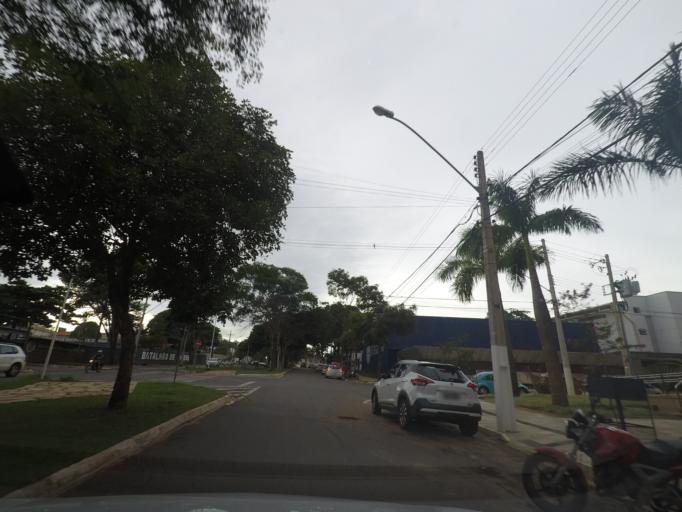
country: BR
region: Goias
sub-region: Goiania
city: Goiania
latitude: -16.7038
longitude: -49.2564
